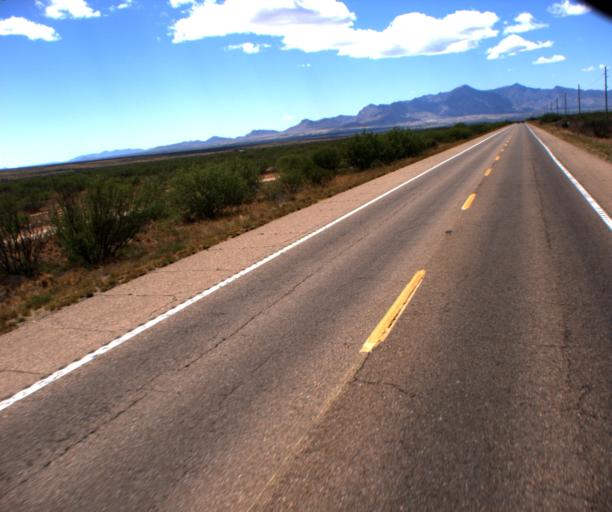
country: US
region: Arizona
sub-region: Cochise County
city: Naco
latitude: 31.3767
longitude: -110.0134
